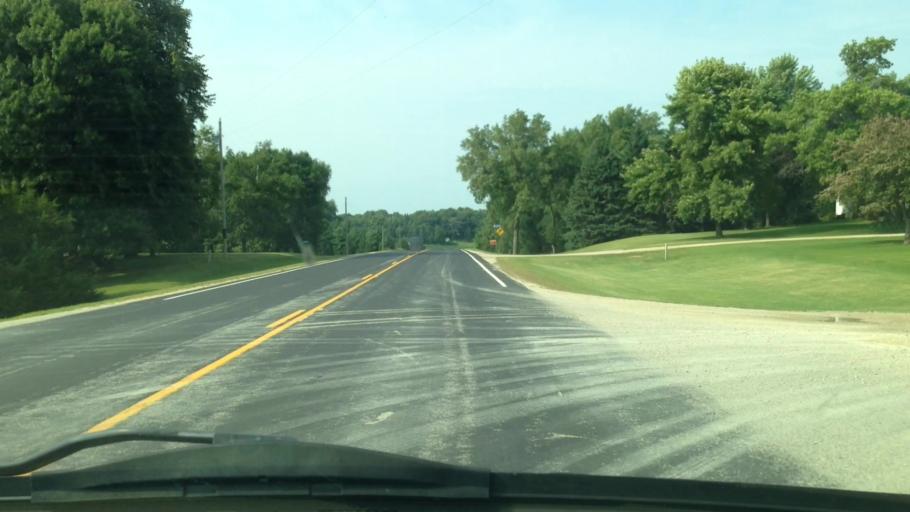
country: US
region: Minnesota
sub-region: Winona County
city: Lewiston
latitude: 43.9625
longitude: -91.9543
